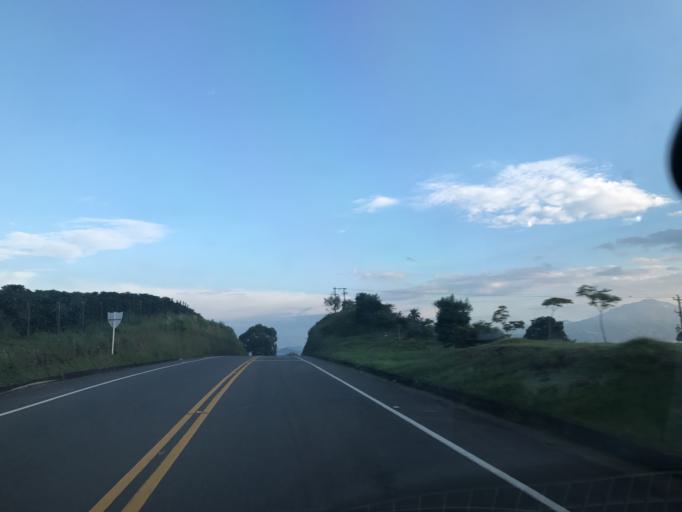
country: CO
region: Risaralda
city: Pereira
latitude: 4.7541
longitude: -75.6992
